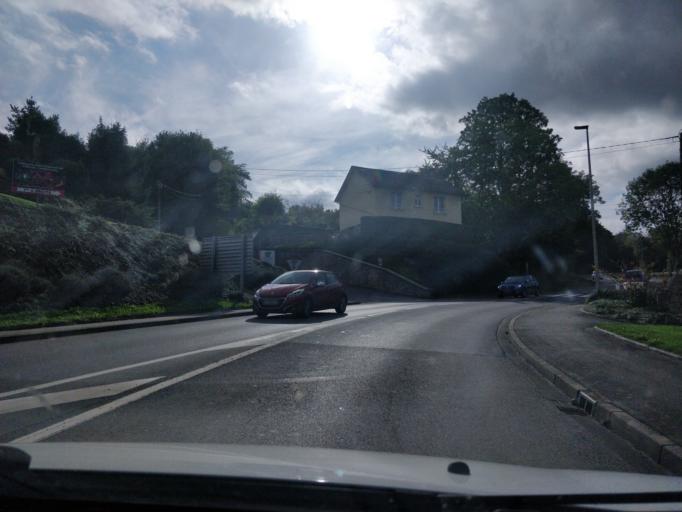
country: FR
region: Lower Normandy
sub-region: Departement du Calvados
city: Vire
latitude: 48.8448
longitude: -0.8954
